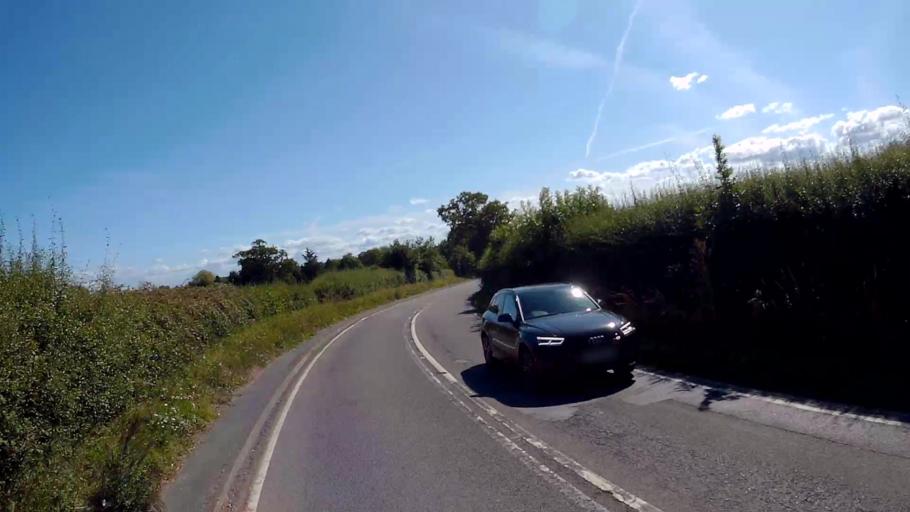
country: GB
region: England
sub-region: Wokingham
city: Swallowfield
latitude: 51.3845
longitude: -0.9693
